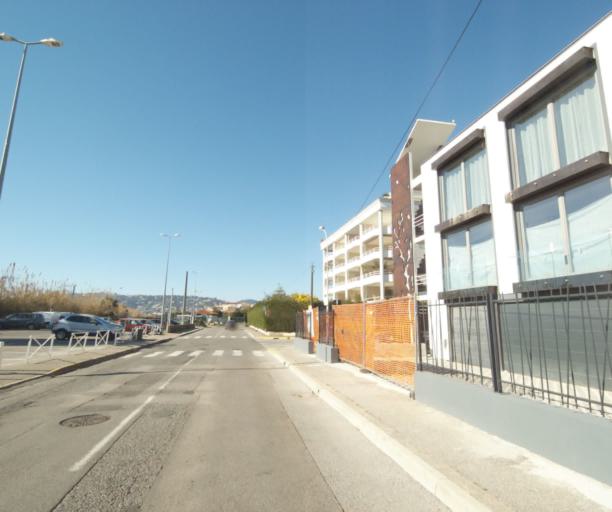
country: FR
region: Provence-Alpes-Cote d'Azur
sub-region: Departement des Alpes-Maritimes
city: Antibes
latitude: 43.5716
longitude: 7.0975
